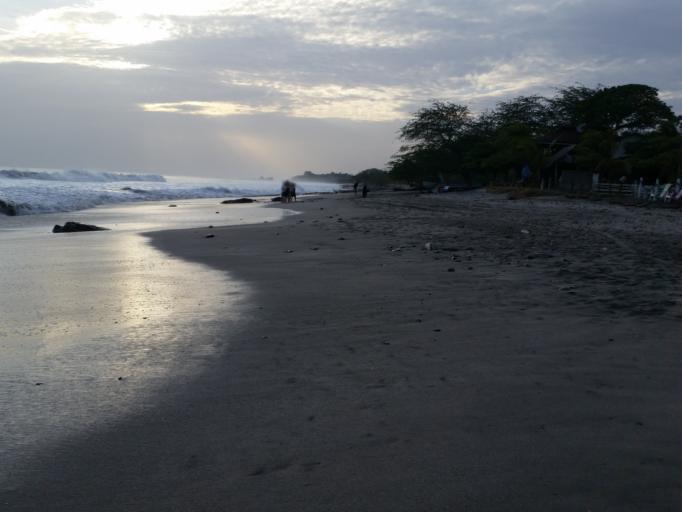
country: NI
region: Rivas
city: Tola
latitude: 11.4442
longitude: -86.0886
